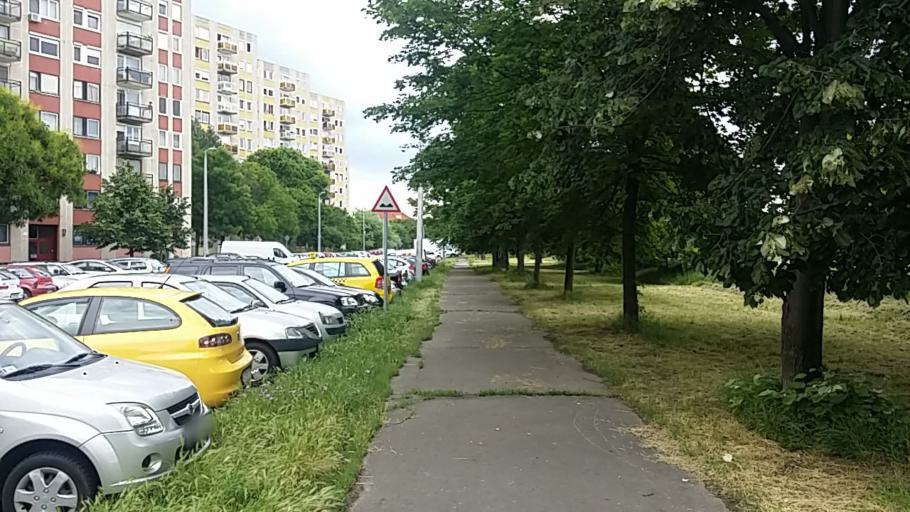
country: HU
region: Budapest
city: Budapest XX. keruelet
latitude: 47.4236
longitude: 19.0897
